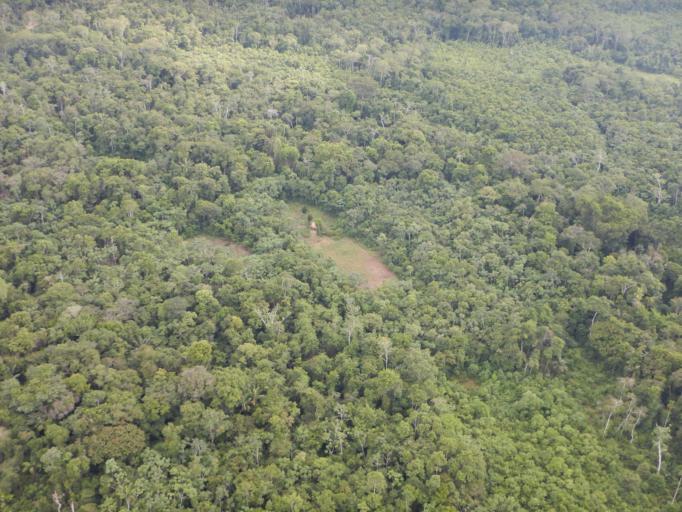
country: BO
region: Cochabamba
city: Chimore
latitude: -16.8945
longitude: -64.8630
